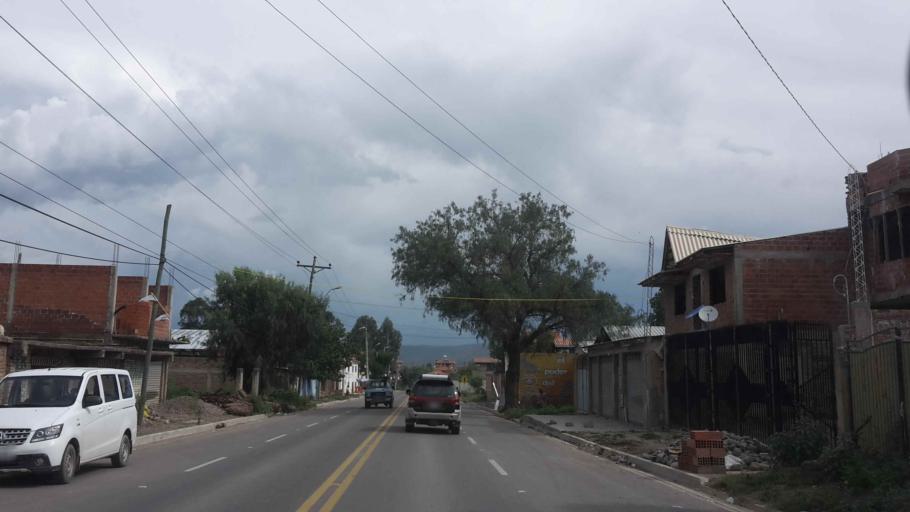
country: BO
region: Cochabamba
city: Cochabamba
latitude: -17.3624
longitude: -66.2529
